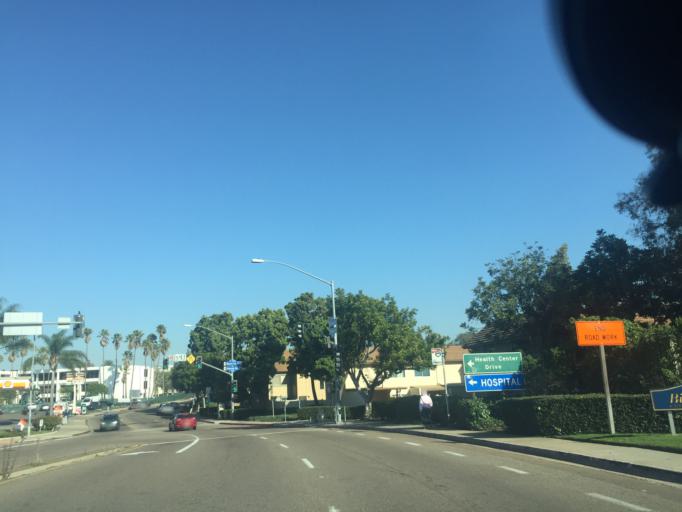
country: US
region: California
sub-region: San Diego County
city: San Diego
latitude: 32.7923
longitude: -117.1568
